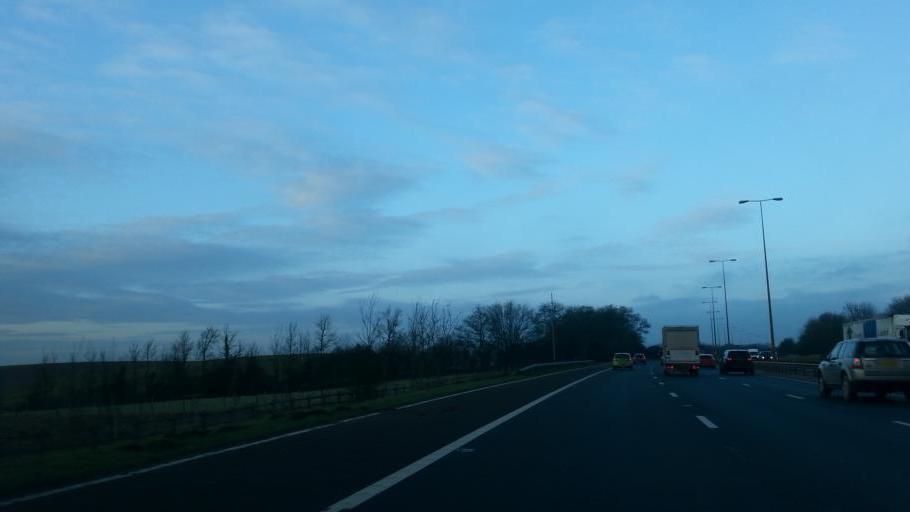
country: GB
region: England
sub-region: Worcestershire
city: Kempsey
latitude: 52.1271
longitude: -2.2009
